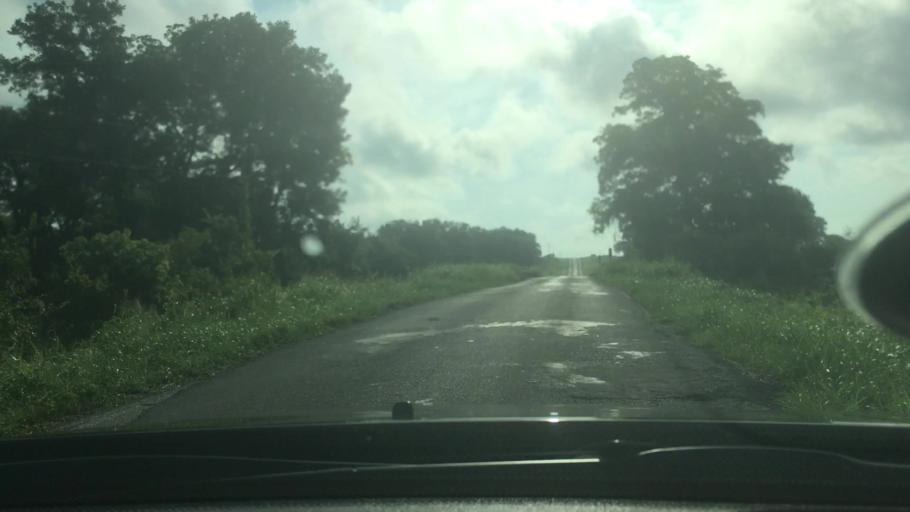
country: US
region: Oklahoma
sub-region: Pontotoc County
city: Ada
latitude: 34.6946
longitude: -96.5426
